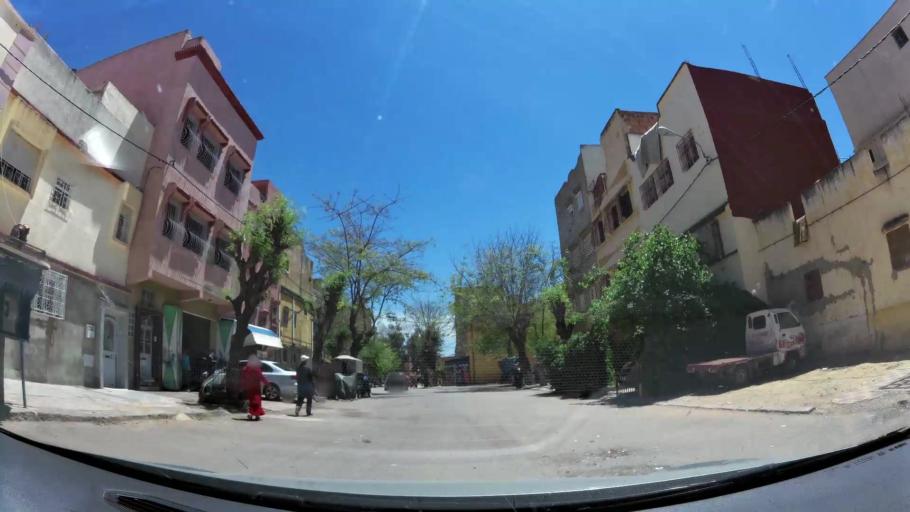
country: MA
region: Meknes-Tafilalet
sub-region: Meknes
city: Meknes
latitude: 33.9118
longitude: -5.5794
